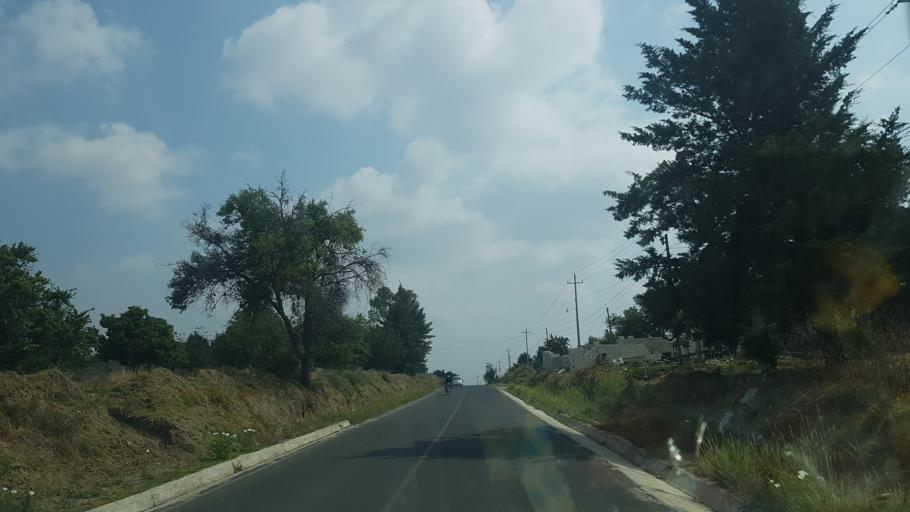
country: MX
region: Puebla
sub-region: Huejotzingo
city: San Juan Pancoac
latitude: 19.1302
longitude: -98.4179
